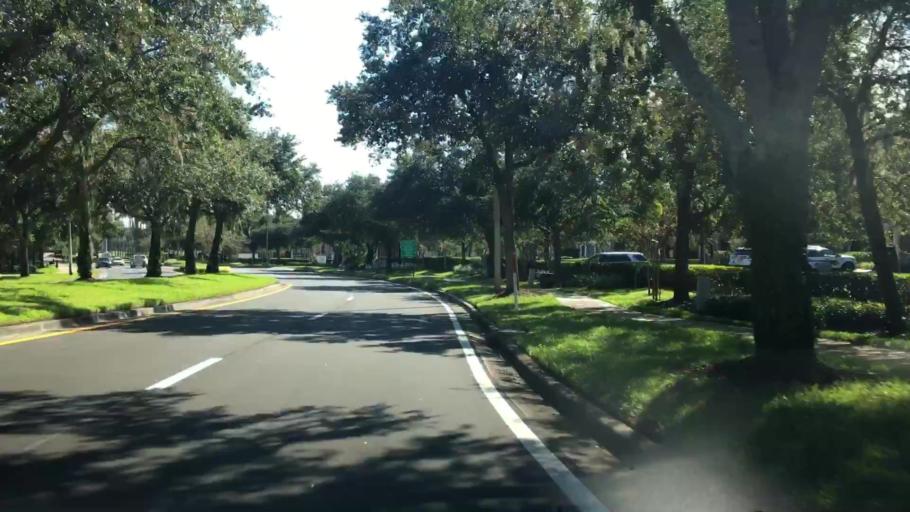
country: US
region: Florida
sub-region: Seminole County
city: Heathrow
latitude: 28.7655
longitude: -81.3502
